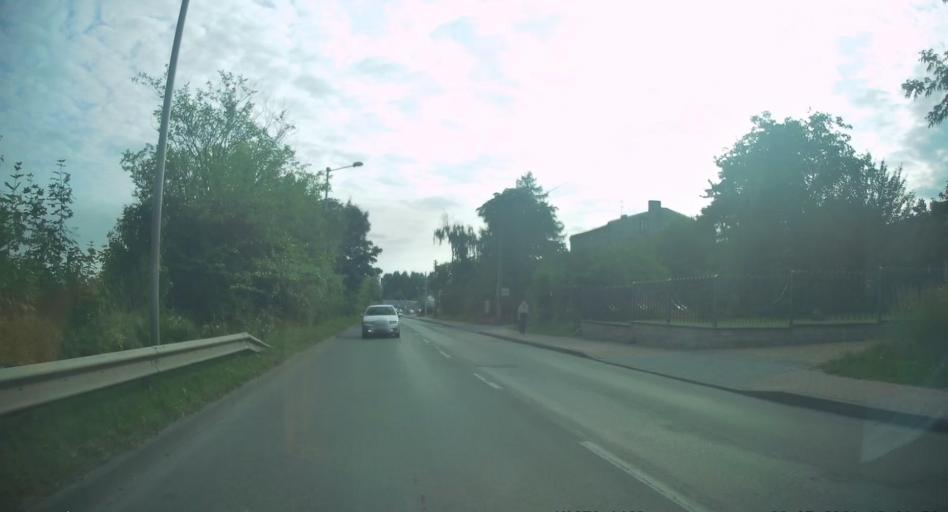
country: PL
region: Silesian Voivodeship
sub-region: Czestochowa
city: Czestochowa
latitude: 50.8272
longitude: 19.1341
